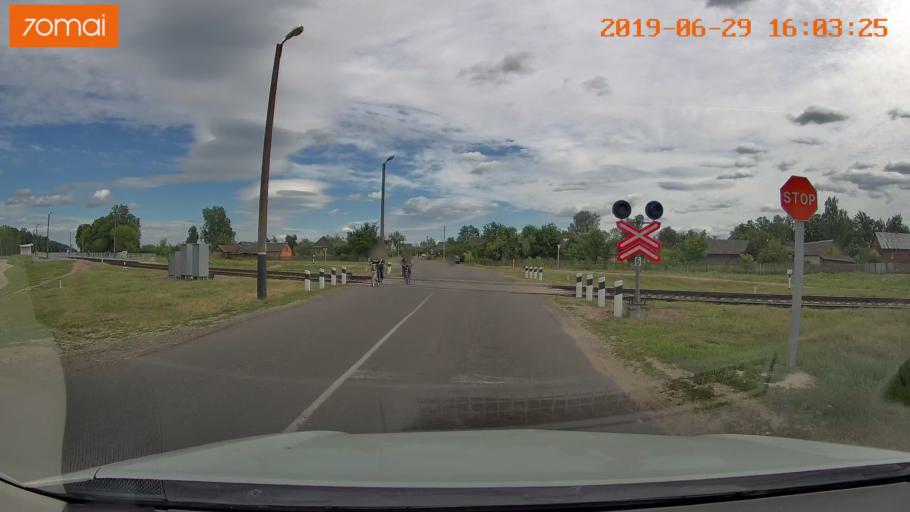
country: BY
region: Brest
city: Luninyets
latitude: 52.2292
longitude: 27.0196
